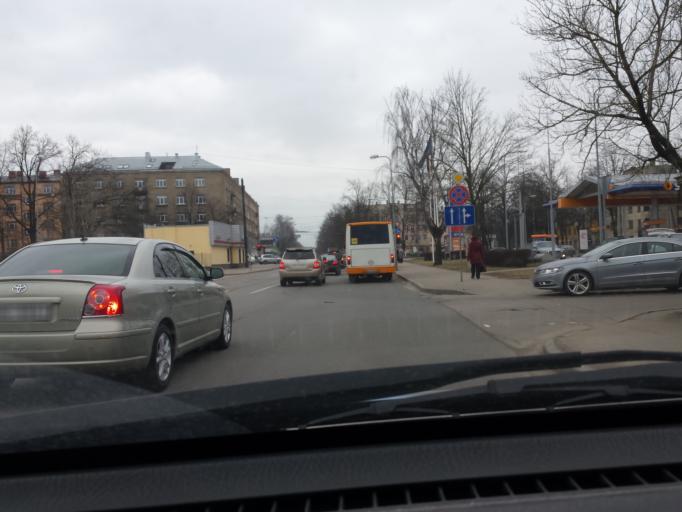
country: LV
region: Riga
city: Jaunciems
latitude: 56.9798
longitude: 24.1845
